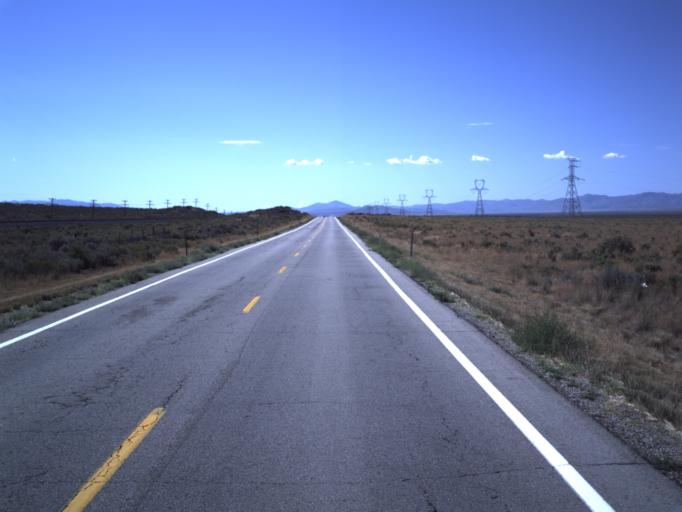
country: US
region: Utah
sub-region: Tooele County
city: Tooele
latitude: 40.3560
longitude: -112.4132
